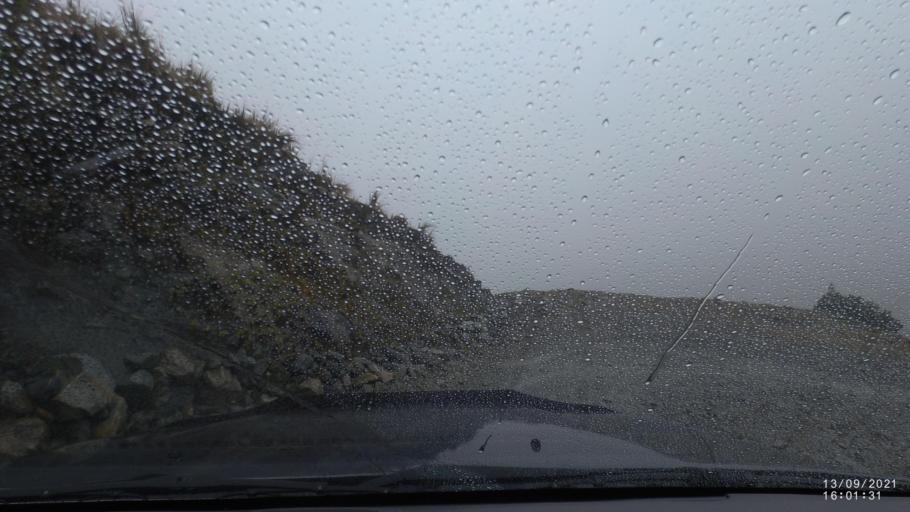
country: BO
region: Cochabamba
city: Colomi
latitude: -17.2933
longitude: -65.7113
